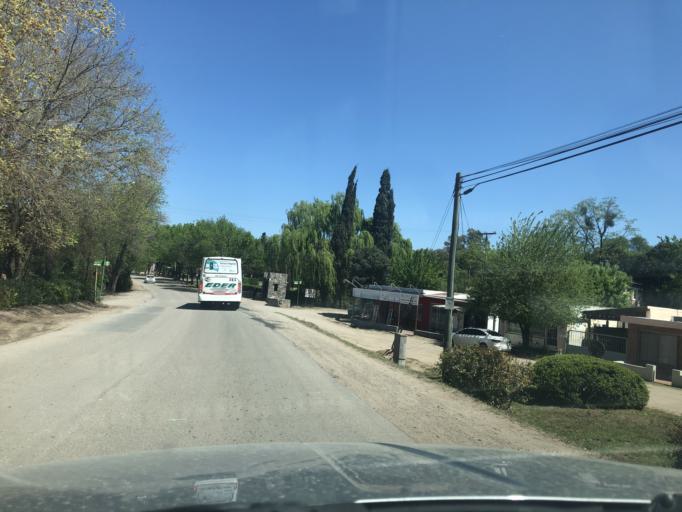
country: AR
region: Cordoba
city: La Granja
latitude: -31.0187
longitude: -64.2739
